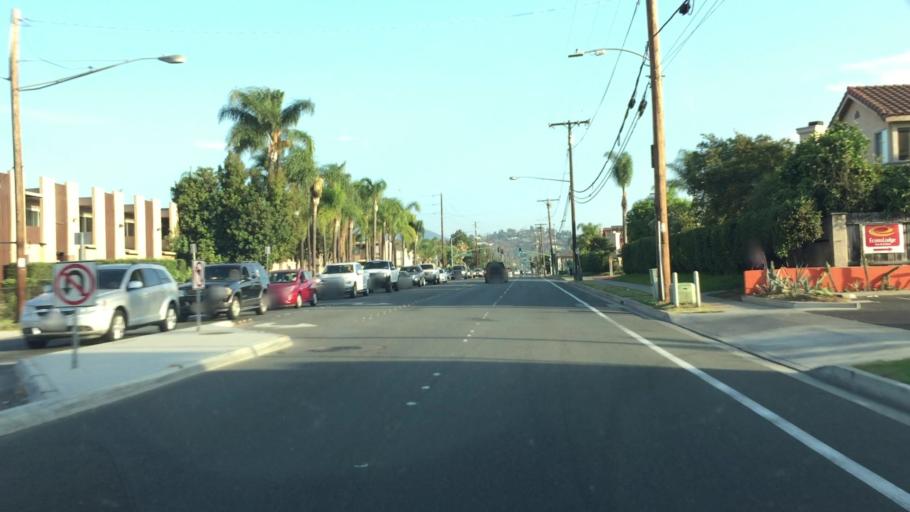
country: US
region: California
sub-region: San Diego County
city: El Cajon
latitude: 32.8021
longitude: -116.9511
